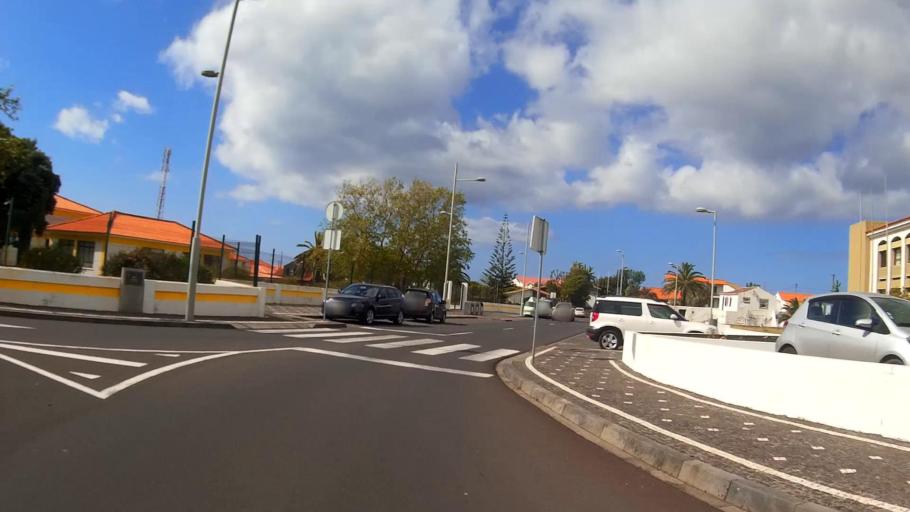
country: PT
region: Azores
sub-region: Madalena
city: Madalena
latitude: 38.5343
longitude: -28.5252
